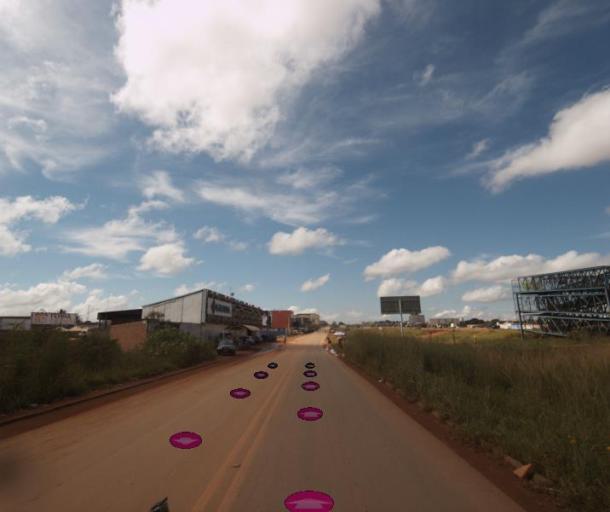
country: BR
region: Federal District
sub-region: Brasilia
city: Brasilia
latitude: -15.7399
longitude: -48.2711
